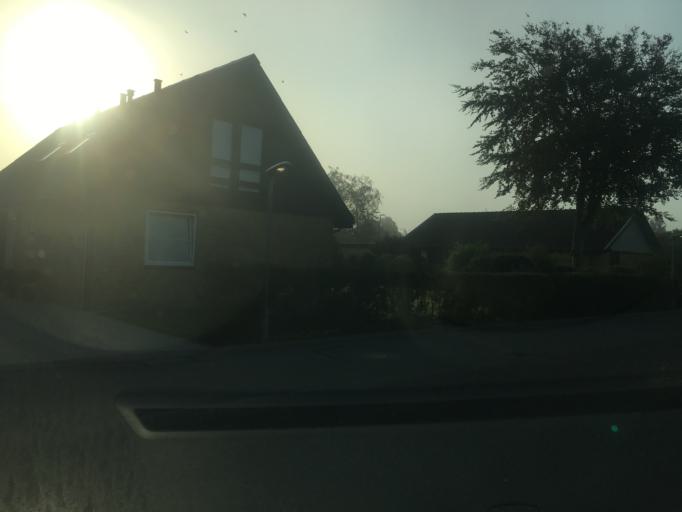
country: DK
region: South Denmark
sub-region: Tonder Kommune
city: Tonder
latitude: 54.9395
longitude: 8.8518
